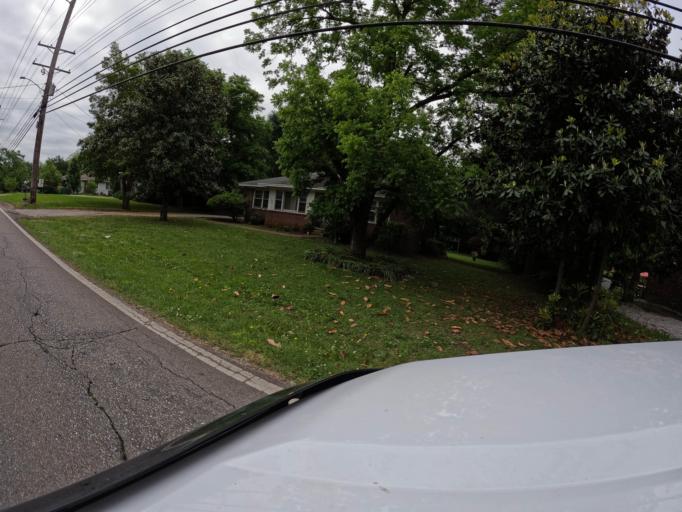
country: US
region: Mississippi
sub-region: Lee County
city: Tupelo
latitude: 34.2648
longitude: -88.7425
